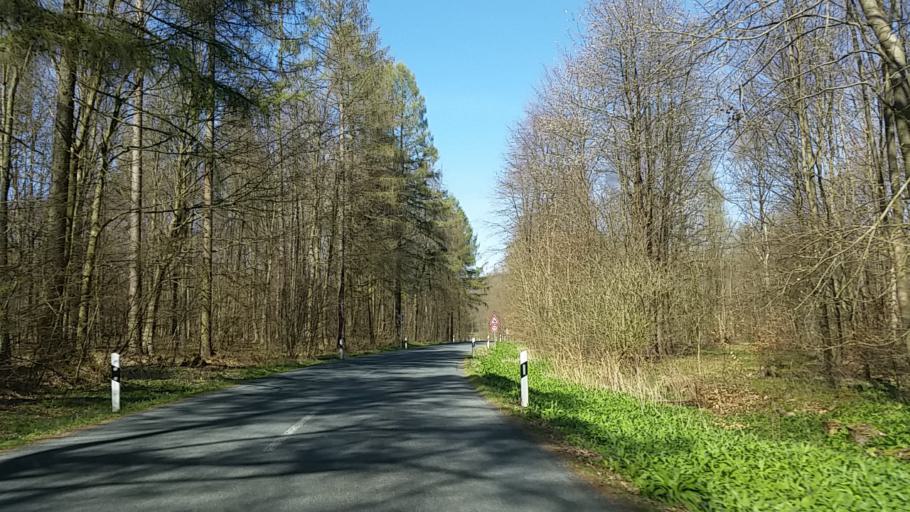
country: DE
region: Lower Saxony
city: Kneitlingen
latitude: 52.1997
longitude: 10.7590
